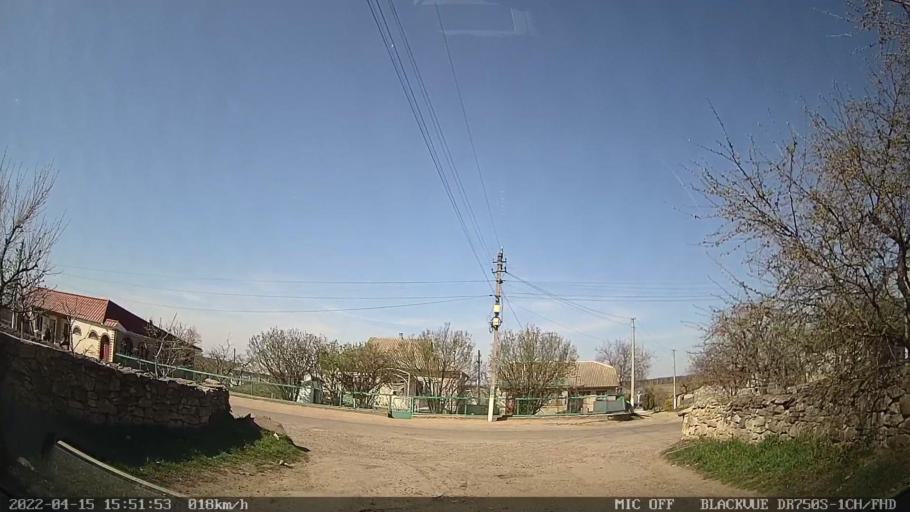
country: MD
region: Raionul Ocnita
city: Otaci
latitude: 48.3955
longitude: 27.8976
